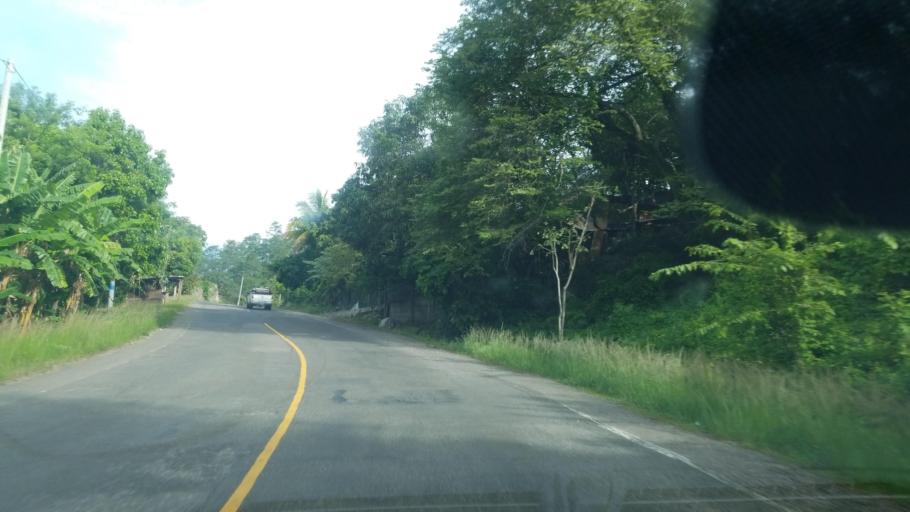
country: HN
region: Santa Barbara
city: Trinidad
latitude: 15.1641
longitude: -88.2609
